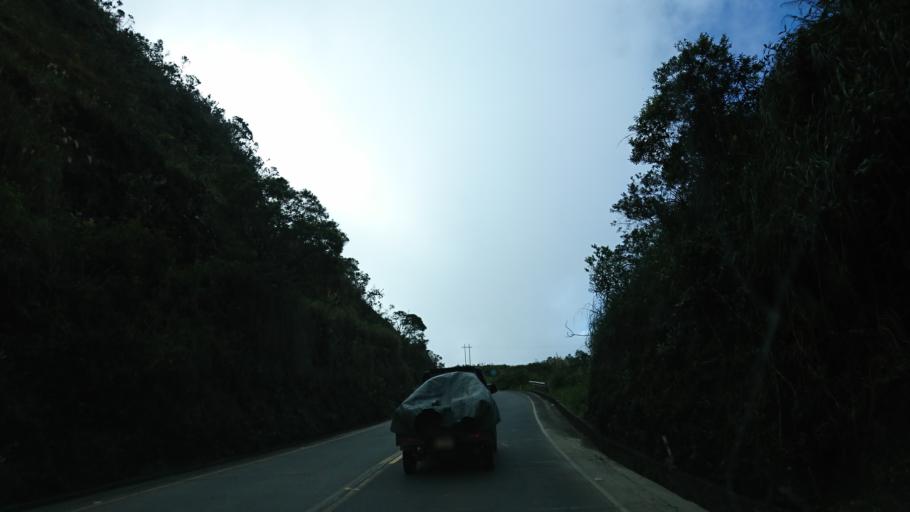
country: BO
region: La Paz
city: Coroico
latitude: -16.2556
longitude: -67.8360
